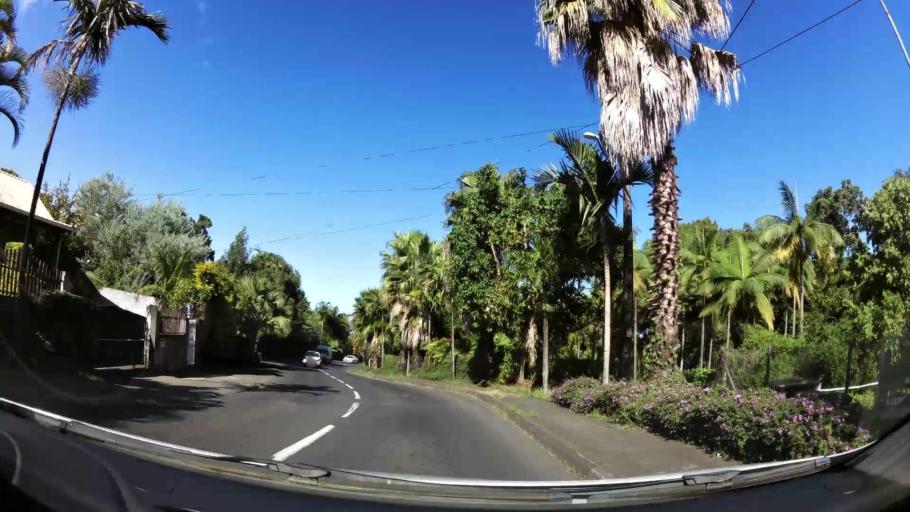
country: RE
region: Reunion
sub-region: Reunion
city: Le Tampon
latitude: -21.2678
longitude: 55.5238
